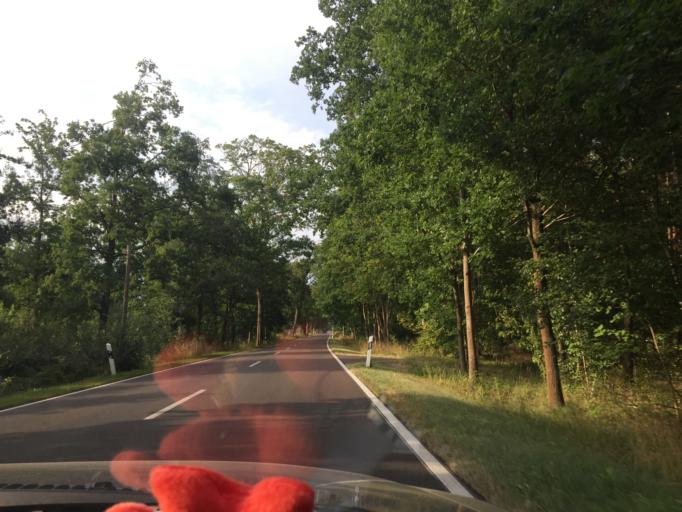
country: DE
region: Brandenburg
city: Liebenwalde
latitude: 52.8858
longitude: 13.3963
